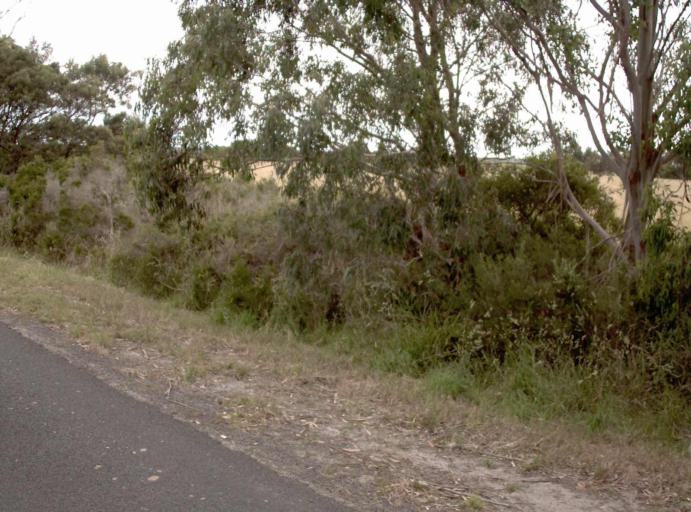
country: AU
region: Victoria
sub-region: Wellington
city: Sale
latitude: -38.6011
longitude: 146.8862
